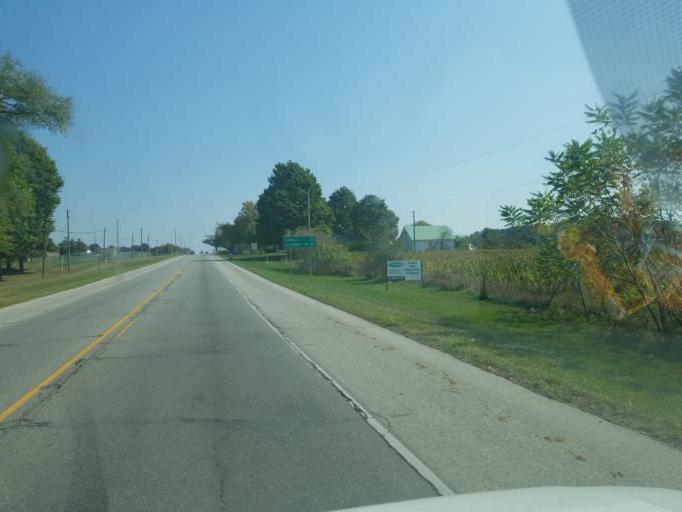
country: US
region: Indiana
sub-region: LaGrange County
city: Lagrange
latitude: 41.6415
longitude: -85.4117
